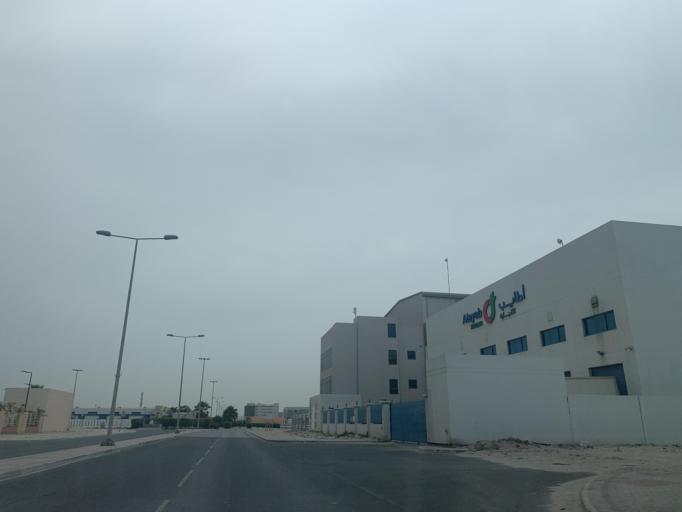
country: BH
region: Muharraq
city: Al Hadd
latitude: 26.2134
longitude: 50.6808
